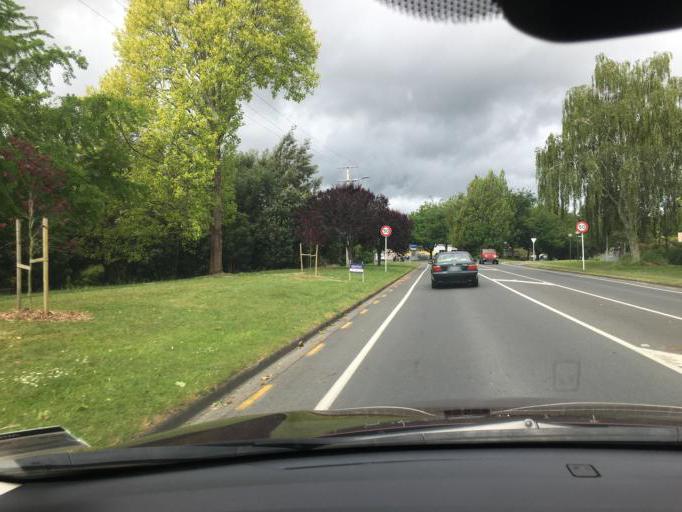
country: NZ
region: Waikato
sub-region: Waipa District
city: Cambridge
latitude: -37.9006
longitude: 175.4708
